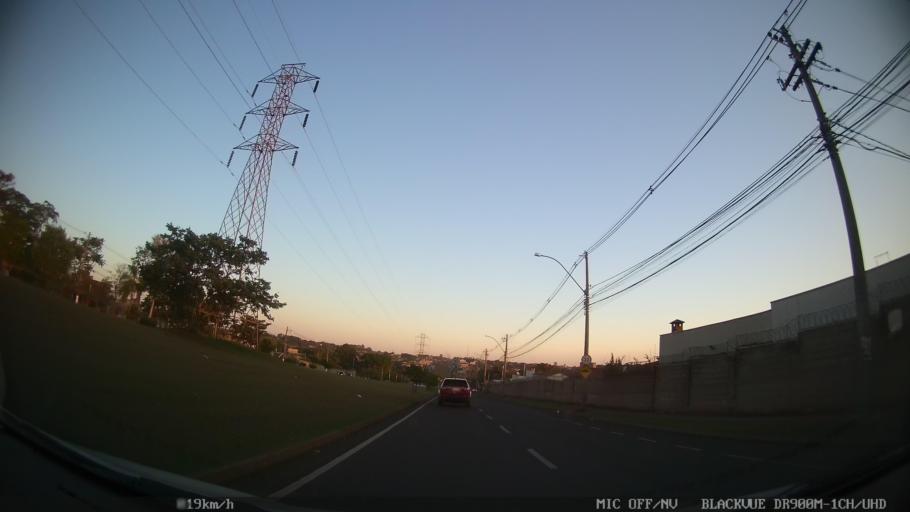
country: BR
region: Sao Paulo
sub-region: Sao Jose Do Rio Preto
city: Sao Jose do Rio Preto
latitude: -20.7819
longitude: -49.3431
